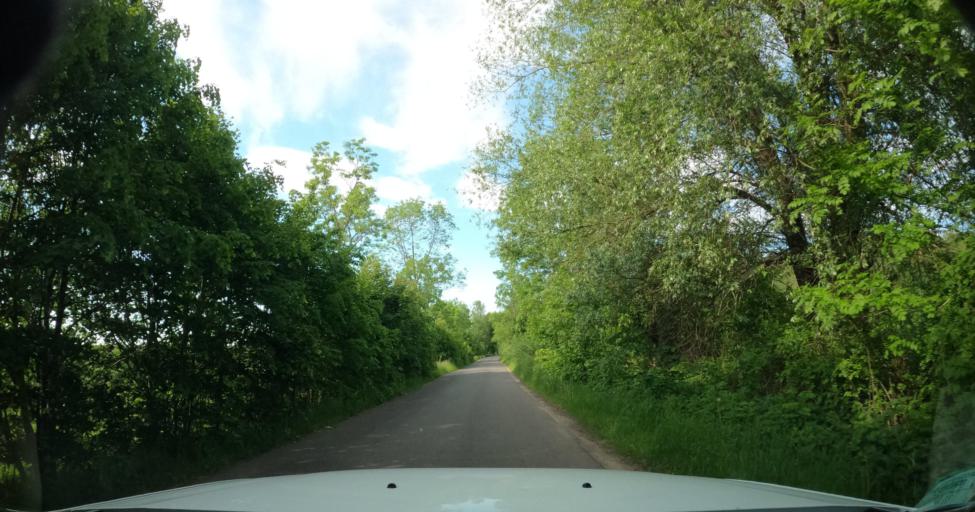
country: PL
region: Warmian-Masurian Voivodeship
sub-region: Powiat ostrodzki
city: Morag
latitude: 54.0685
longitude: 19.8897
